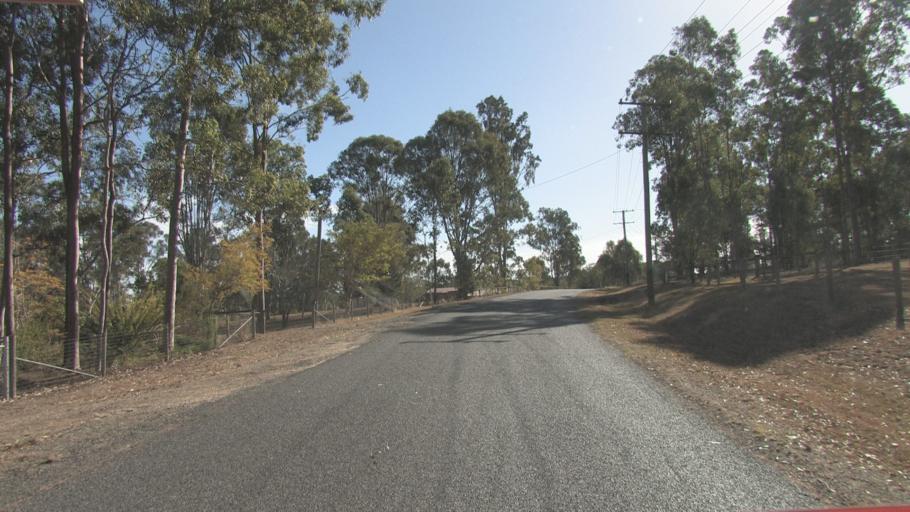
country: AU
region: Queensland
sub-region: Logan
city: Cedar Vale
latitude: -27.8700
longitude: 152.9832
